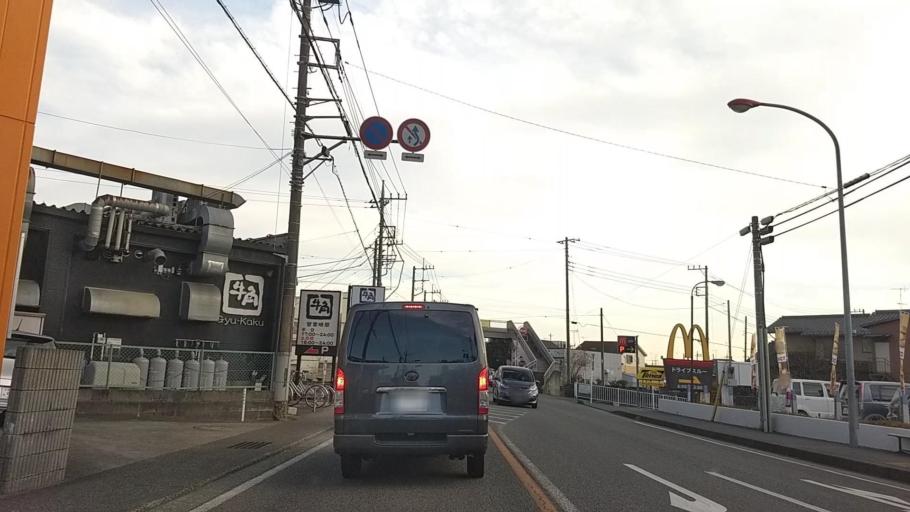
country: JP
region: Kanagawa
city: Atsugi
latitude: 35.4654
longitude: 139.3550
